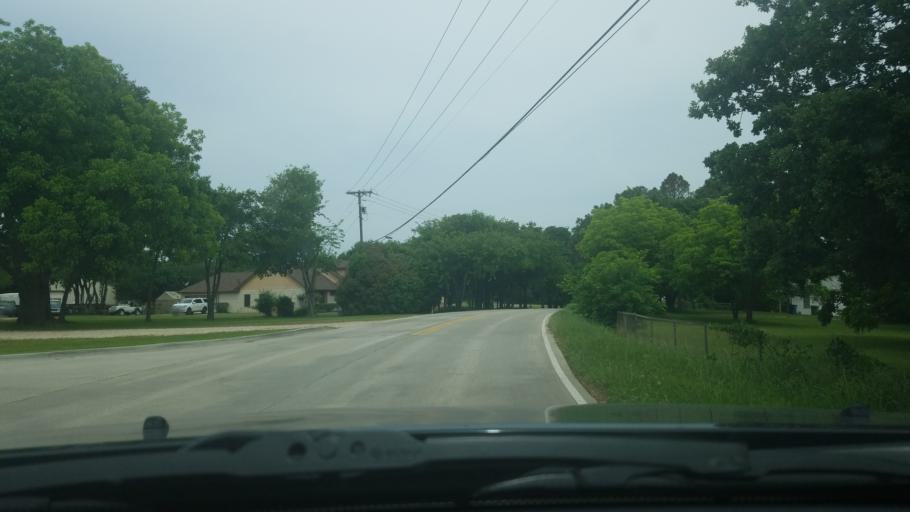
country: US
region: Texas
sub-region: Denton County
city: Lake Dallas
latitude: 33.1106
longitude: -97.0175
